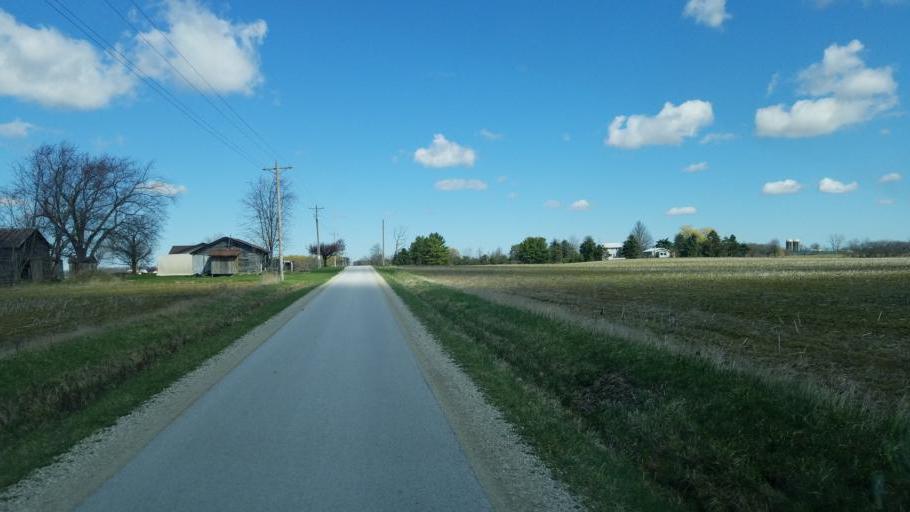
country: US
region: Ohio
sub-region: Sandusky County
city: Mount Carmel
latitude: 41.2204
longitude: -82.9372
